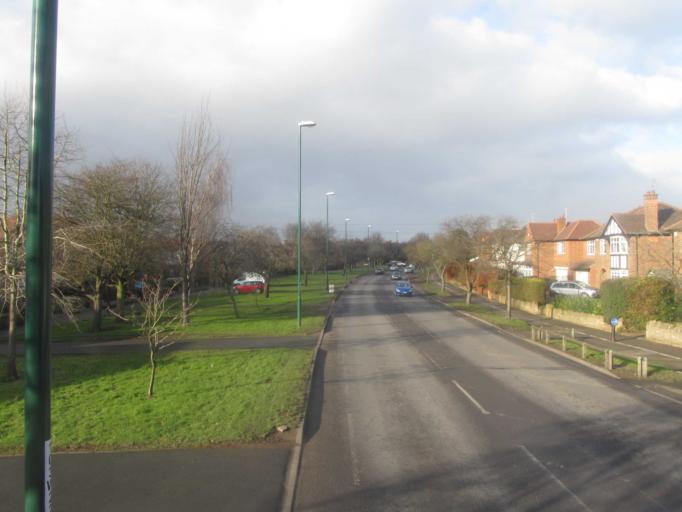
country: GB
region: England
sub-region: Nottinghamshire
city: Kimberley
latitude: 52.9424
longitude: -1.2230
